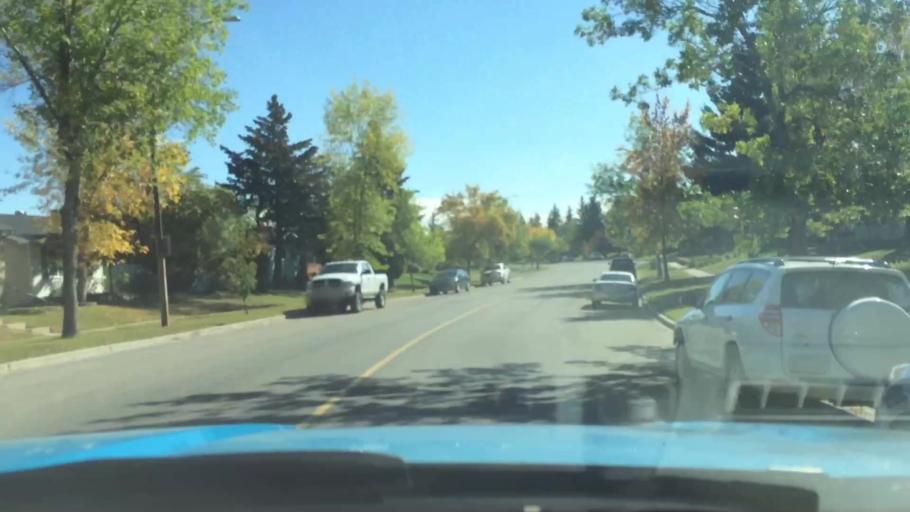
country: CA
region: Alberta
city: Calgary
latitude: 51.1183
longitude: -114.0649
